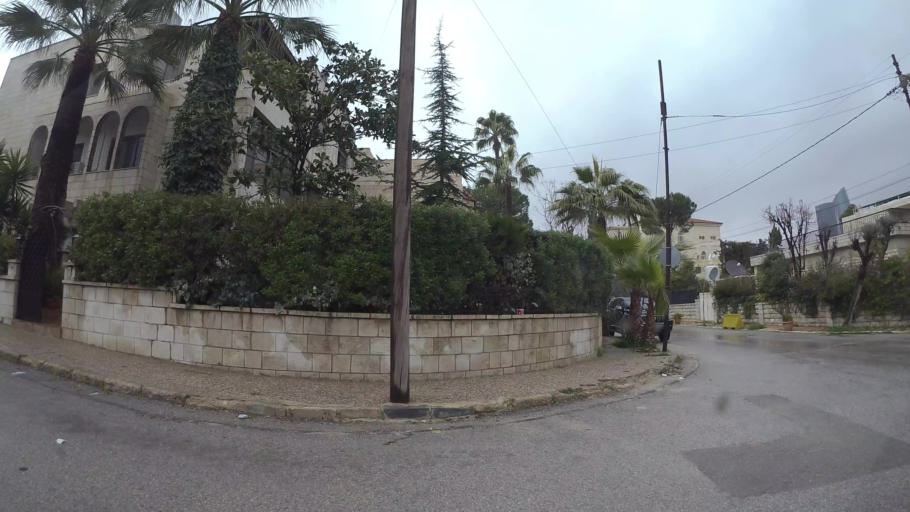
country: JO
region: Amman
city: Amman
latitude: 31.9568
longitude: 35.9049
